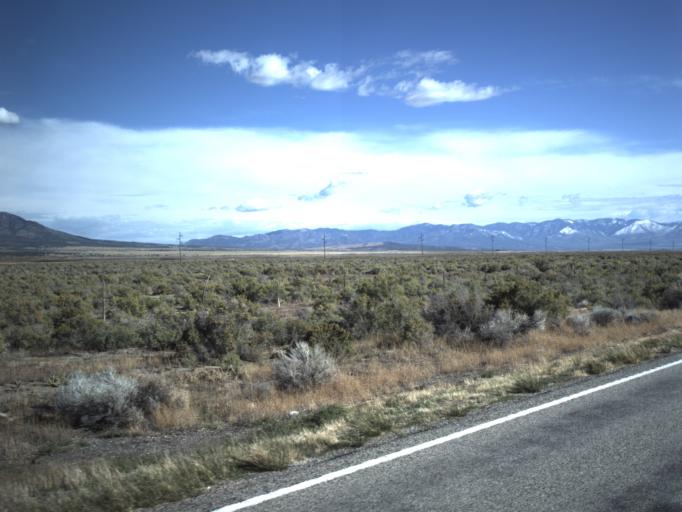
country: US
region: Utah
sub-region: Millard County
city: Delta
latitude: 39.2816
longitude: -112.4607
